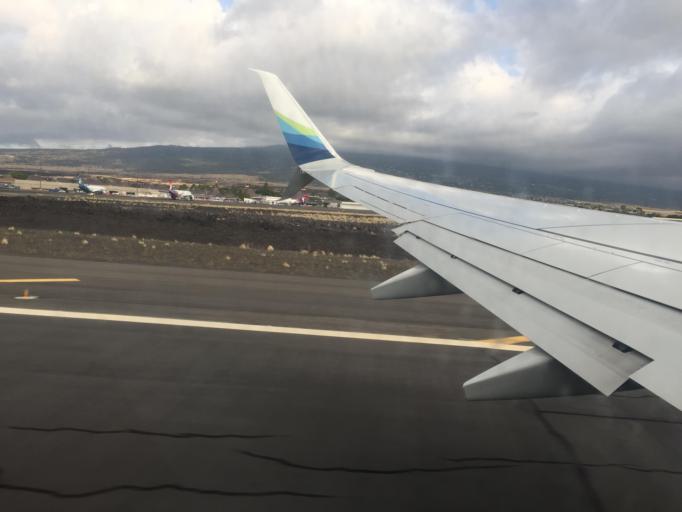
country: US
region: Hawaii
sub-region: Hawaii County
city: Kalaoa
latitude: 19.7348
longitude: -156.0460
